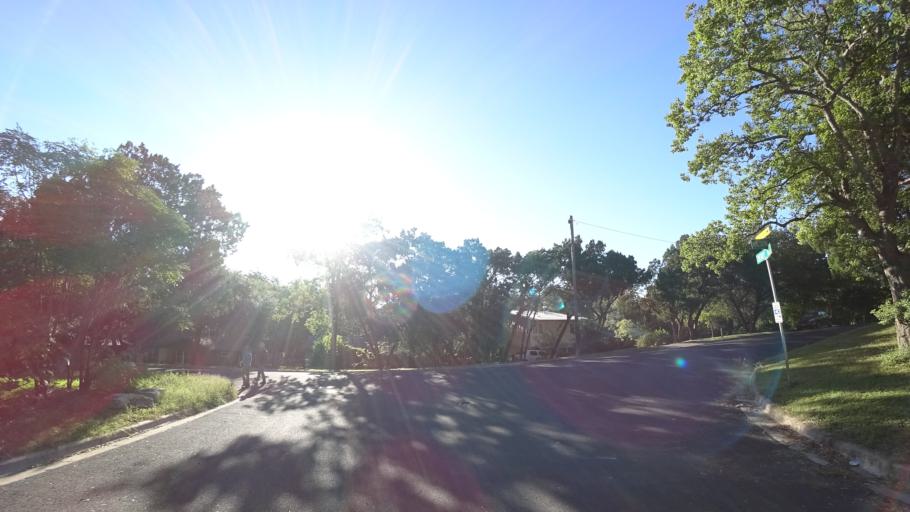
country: US
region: Texas
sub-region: Travis County
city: Austin
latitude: 30.2282
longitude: -97.7648
